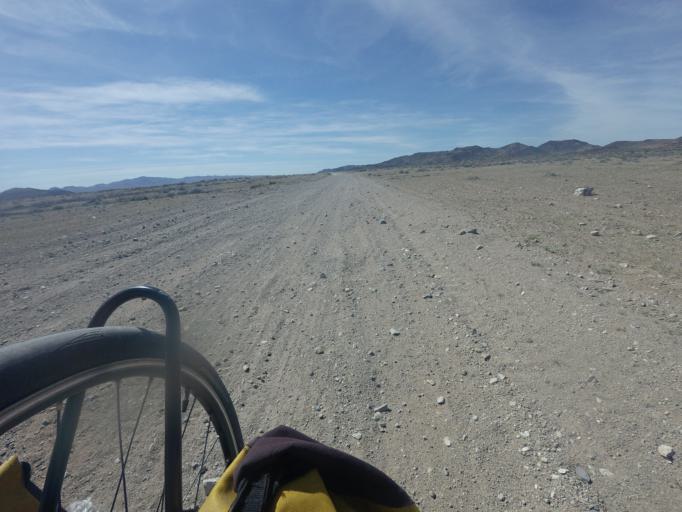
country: US
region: California
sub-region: San Bernardino County
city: Searles Valley
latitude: 35.5931
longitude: -117.4119
